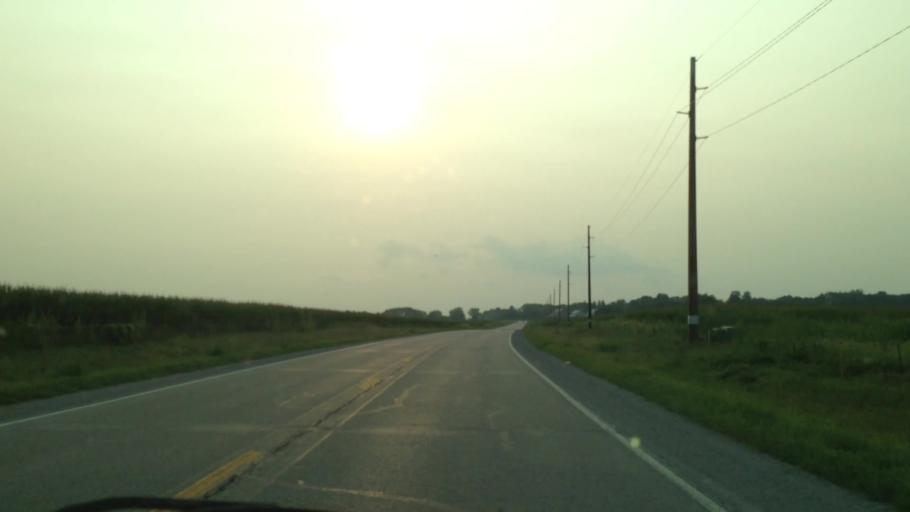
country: US
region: Iowa
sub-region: Iowa County
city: Marengo
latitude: 41.8032
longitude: -91.9491
